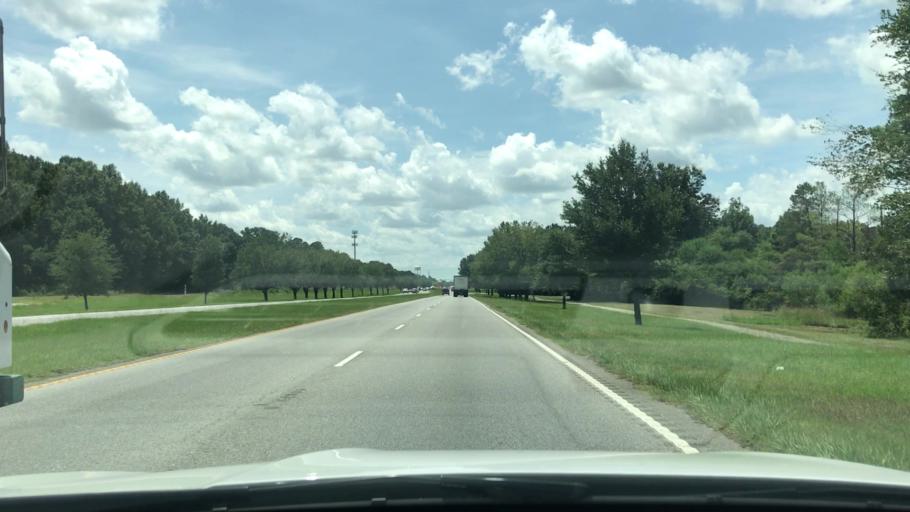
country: US
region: South Carolina
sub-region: Berkeley County
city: Goose Creek
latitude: 33.0239
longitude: -80.0355
